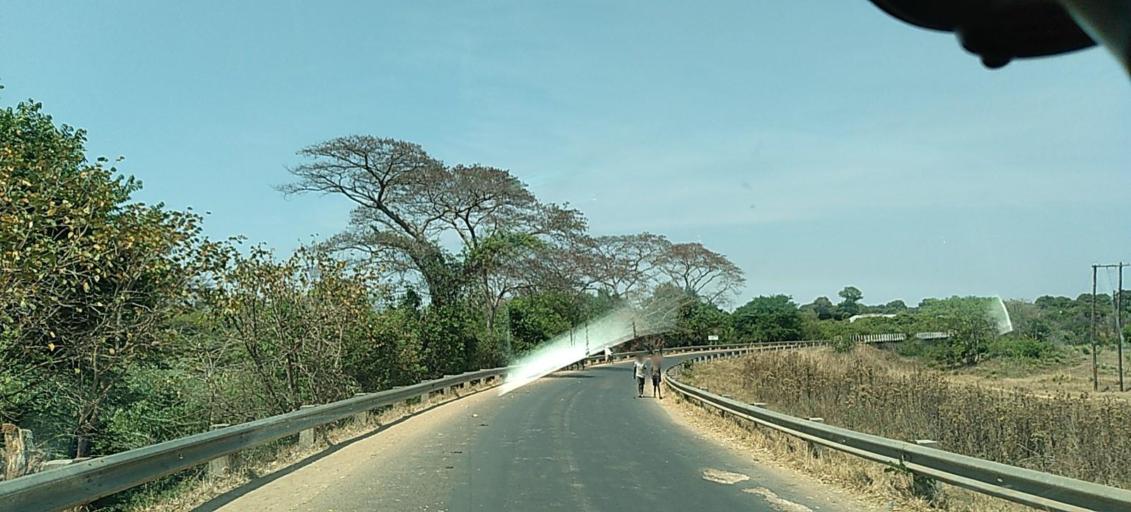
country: ZM
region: North-Western
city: Kabompo
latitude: -13.4127
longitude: 24.3711
